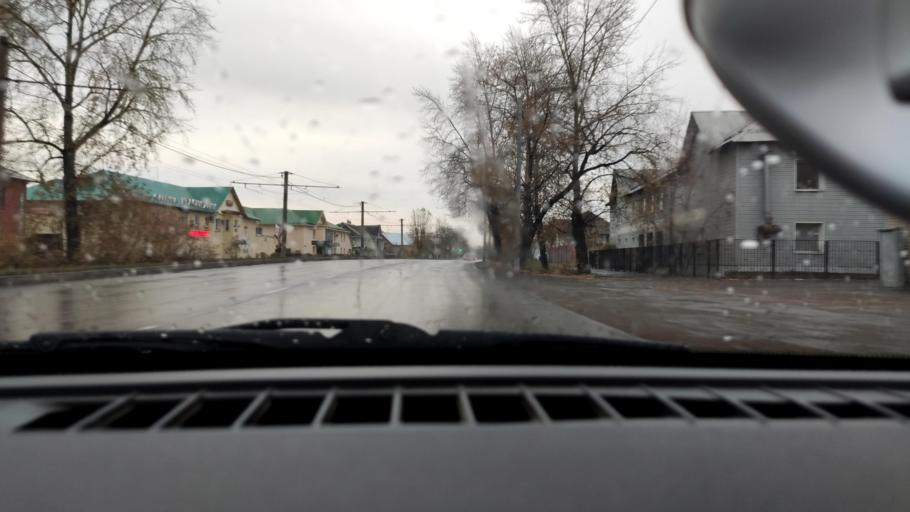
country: RU
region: Perm
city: Kondratovo
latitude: 57.9506
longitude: 56.1315
